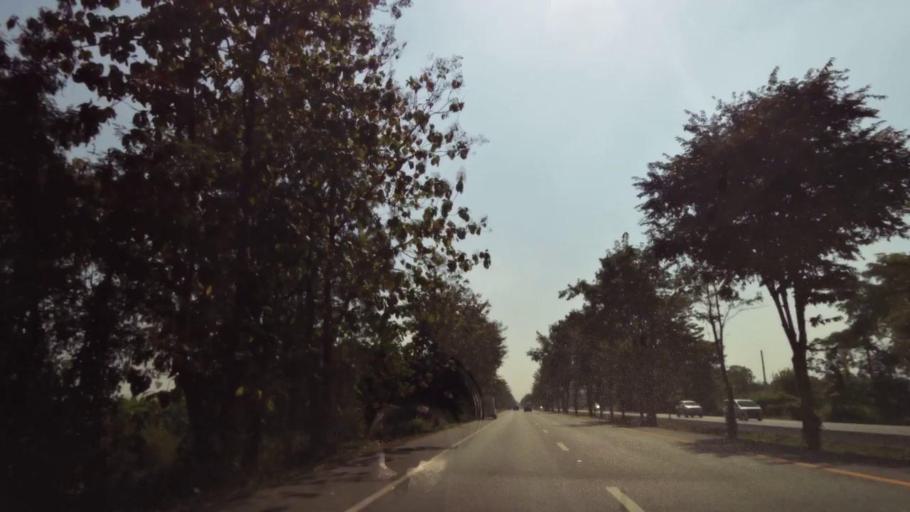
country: TH
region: Phichit
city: Bueng Na Rang
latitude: 16.0806
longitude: 100.1245
